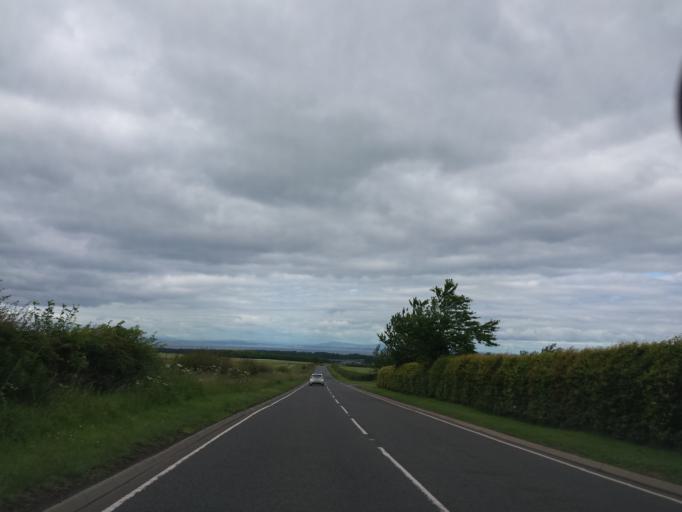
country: GB
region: Scotland
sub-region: East Lothian
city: Haddington
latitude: 55.9795
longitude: -2.8160
